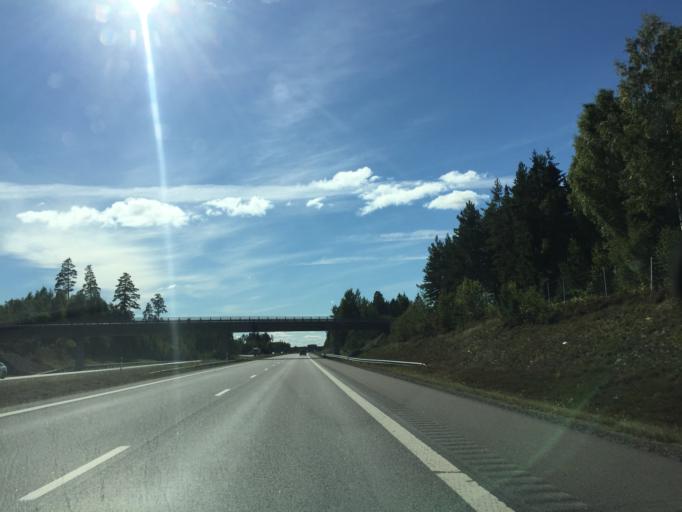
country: SE
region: OErebro
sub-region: Lindesbergs Kommun
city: Fellingsbro
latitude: 59.3459
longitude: 15.5502
